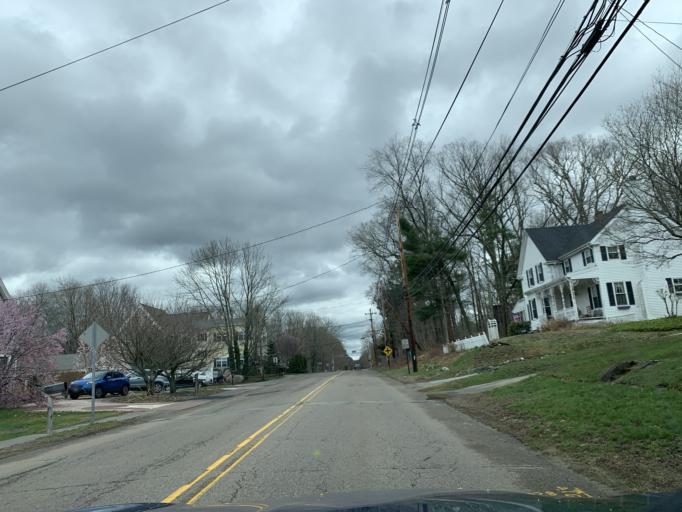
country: US
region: Massachusetts
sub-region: Bristol County
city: Norton
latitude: 41.9468
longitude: -71.2226
